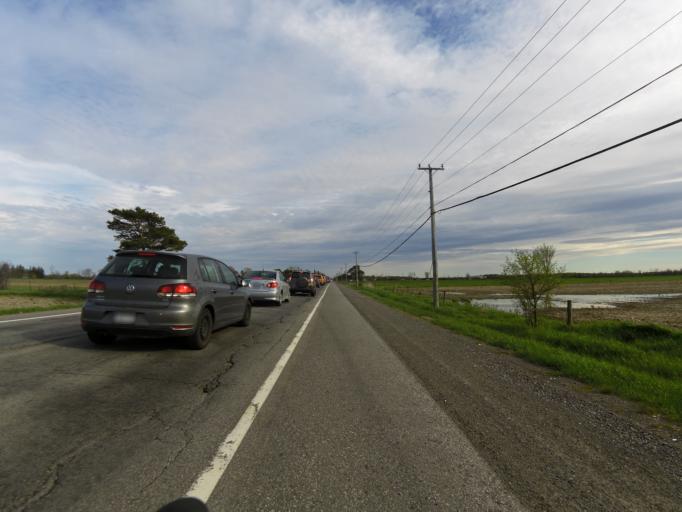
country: CA
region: Ontario
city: Ottawa
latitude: 45.3106
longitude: -75.7103
